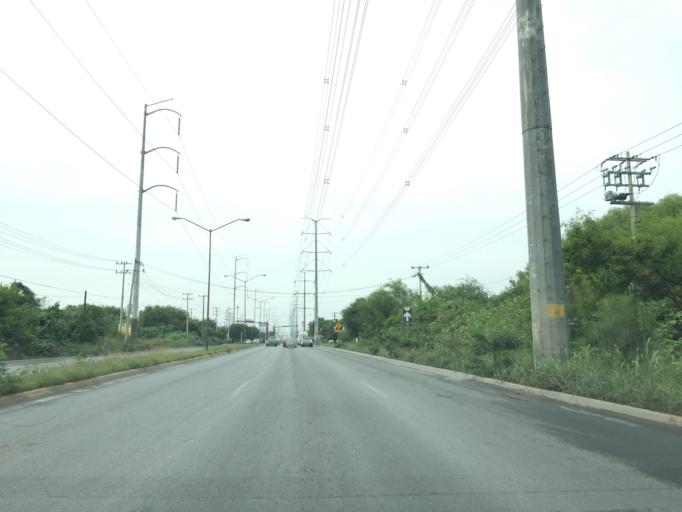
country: MX
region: Nuevo Leon
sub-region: Apodaca
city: Fraccionamiento Cosmopolis Octavo Sector
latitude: 25.7943
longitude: -100.2235
